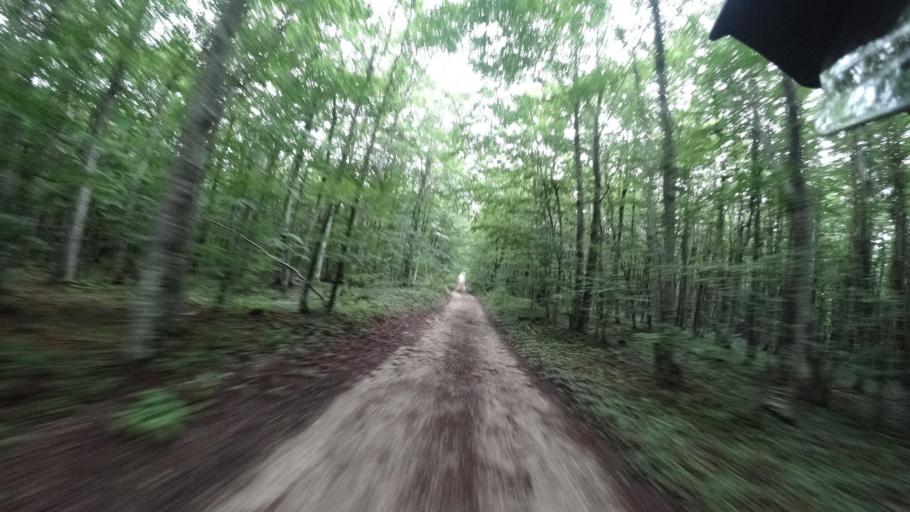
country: BA
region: Federation of Bosnia and Herzegovina
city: Orasac
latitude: 44.5016
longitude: 15.9730
